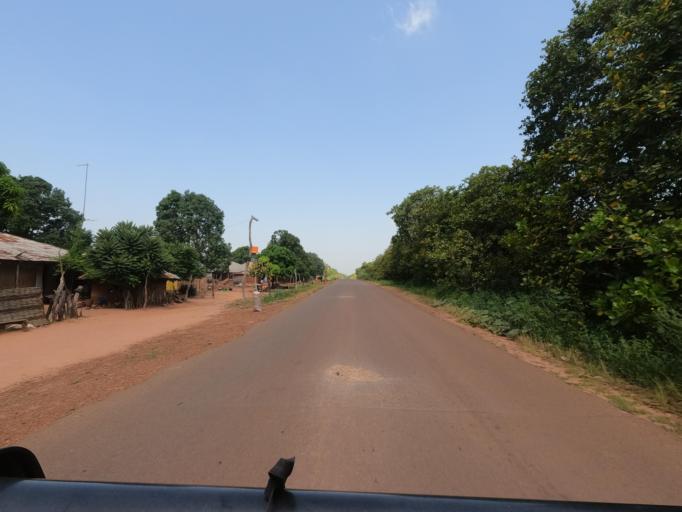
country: SN
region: Ziguinchor
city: Adeane
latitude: 12.3728
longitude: -15.7769
